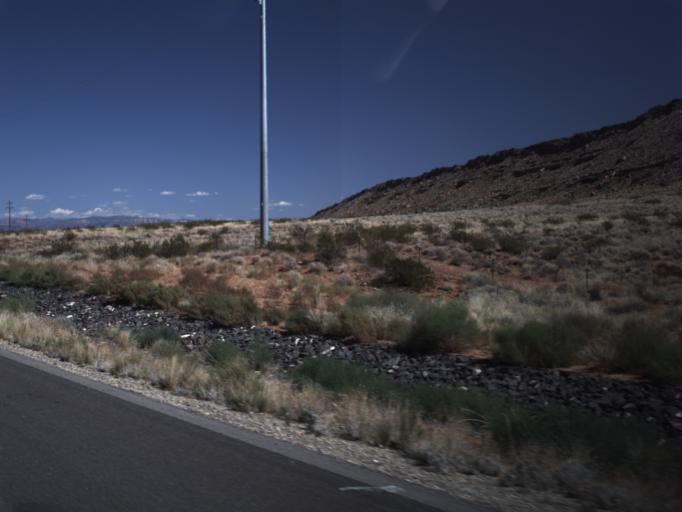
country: US
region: Utah
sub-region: Washington County
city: Washington
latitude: 37.0935
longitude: -113.4701
